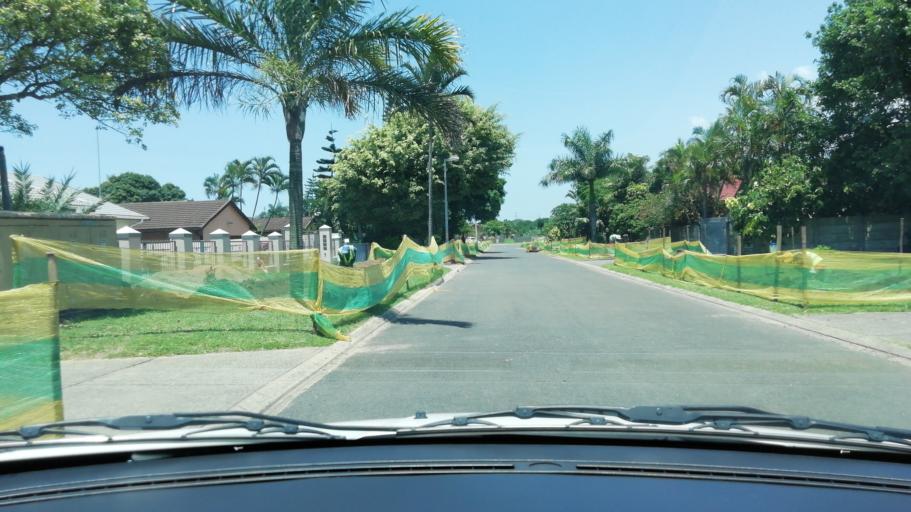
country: ZA
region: KwaZulu-Natal
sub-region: uThungulu District Municipality
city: Richards Bay
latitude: -28.7343
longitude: 32.0597
